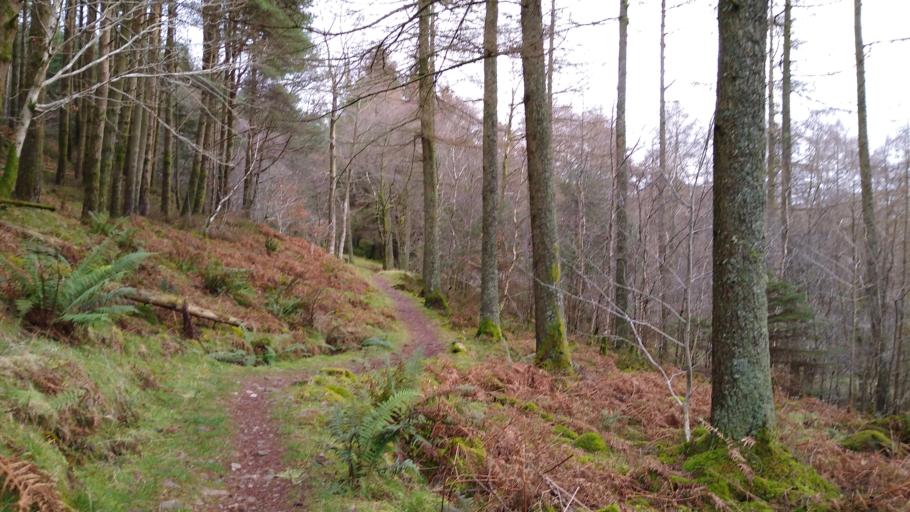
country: GB
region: England
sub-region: Cumbria
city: Frizington
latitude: 54.5223
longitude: -3.3625
